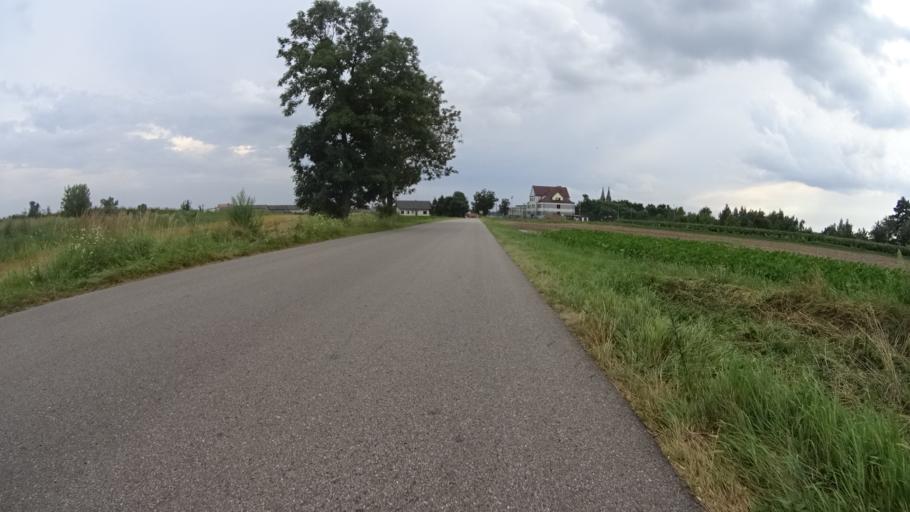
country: PL
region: Masovian Voivodeship
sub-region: Powiat bialobrzeski
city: Wysmierzyce
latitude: 51.6676
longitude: 20.8561
